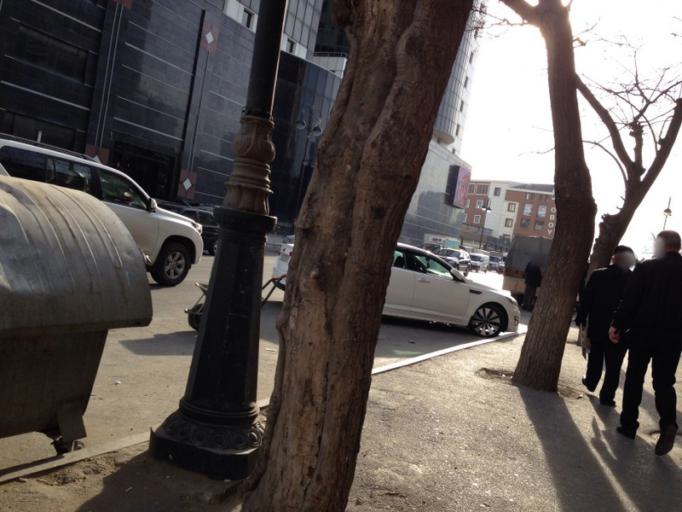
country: AZ
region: Baki
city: Baku
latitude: 40.3906
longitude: 49.8609
